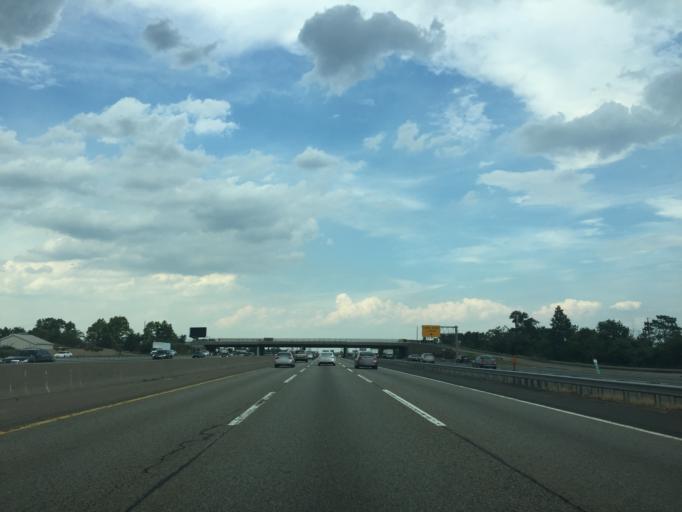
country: US
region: New Jersey
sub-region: Union County
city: Linden
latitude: 40.6094
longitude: -74.2252
